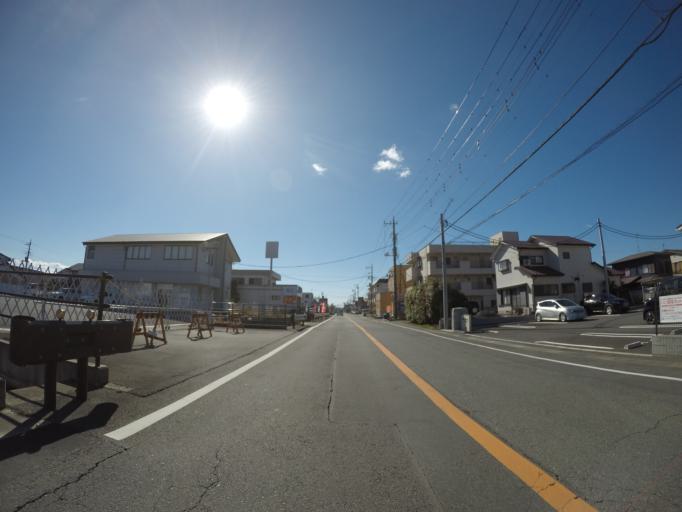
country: JP
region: Shizuoka
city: Numazu
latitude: 35.1378
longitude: 138.8052
